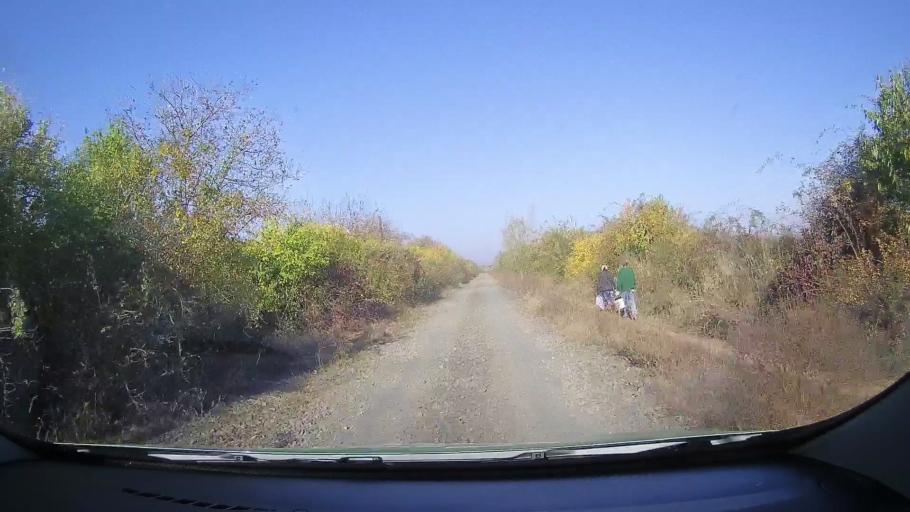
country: RO
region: Satu Mare
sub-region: Comuna Sauca
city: Sauca
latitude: 47.4748
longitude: 22.4796
